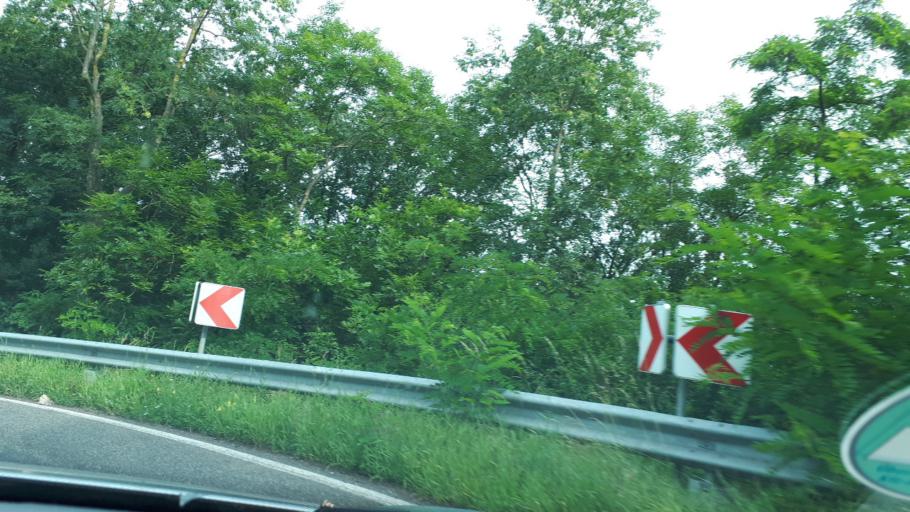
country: DE
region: Rheinland-Pfalz
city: Trimbs
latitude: 50.3216
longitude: 7.3010
